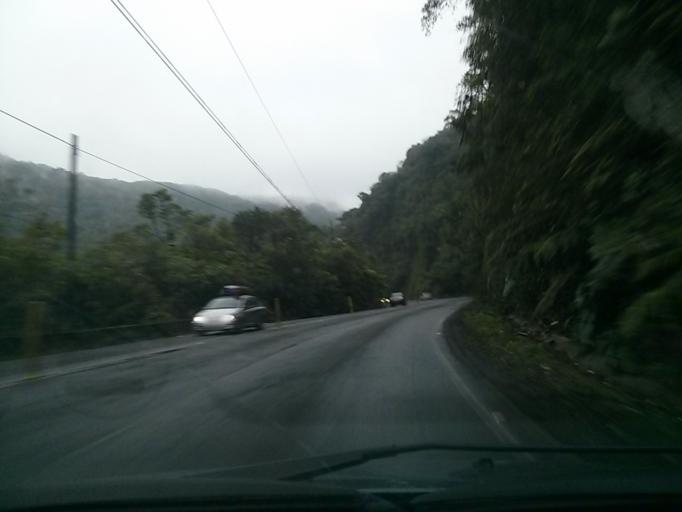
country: CR
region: Heredia
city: Angeles
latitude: 10.0574
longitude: -84.0108
